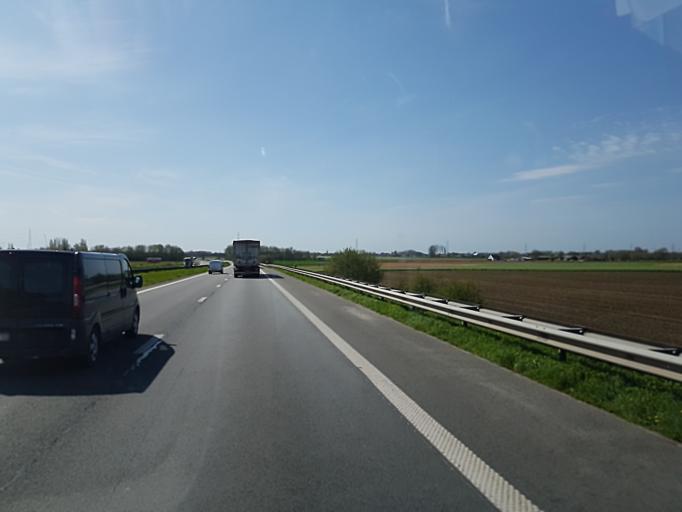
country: BE
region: Wallonia
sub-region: Province du Hainaut
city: Estaimpuis
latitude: 50.6682
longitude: 3.2881
